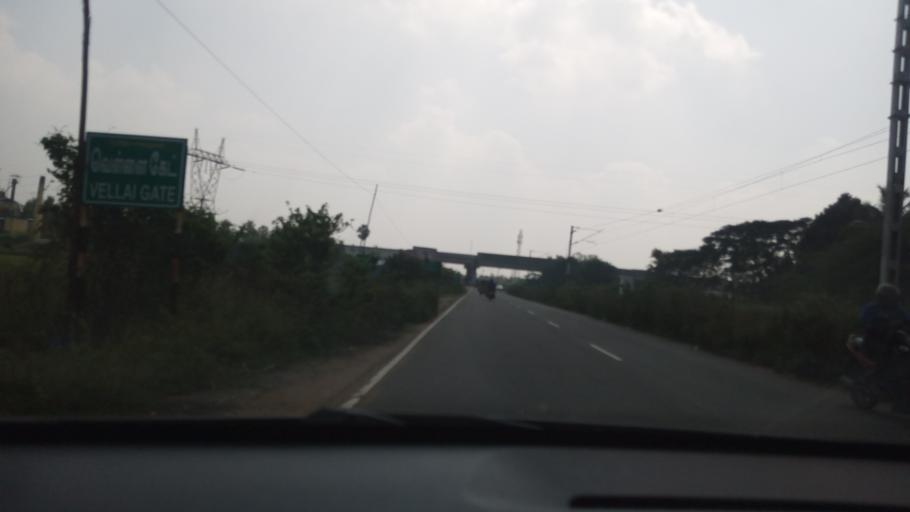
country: IN
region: Tamil Nadu
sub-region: Kancheepuram
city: Kanchipuram
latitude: 12.8764
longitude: 79.6901
